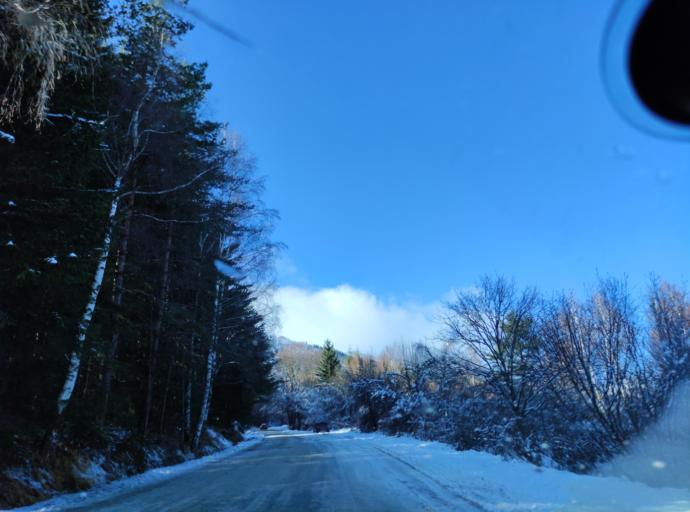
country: BG
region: Sofia-Capital
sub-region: Stolichna Obshtina
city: Sofia
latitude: 42.6043
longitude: 23.3042
